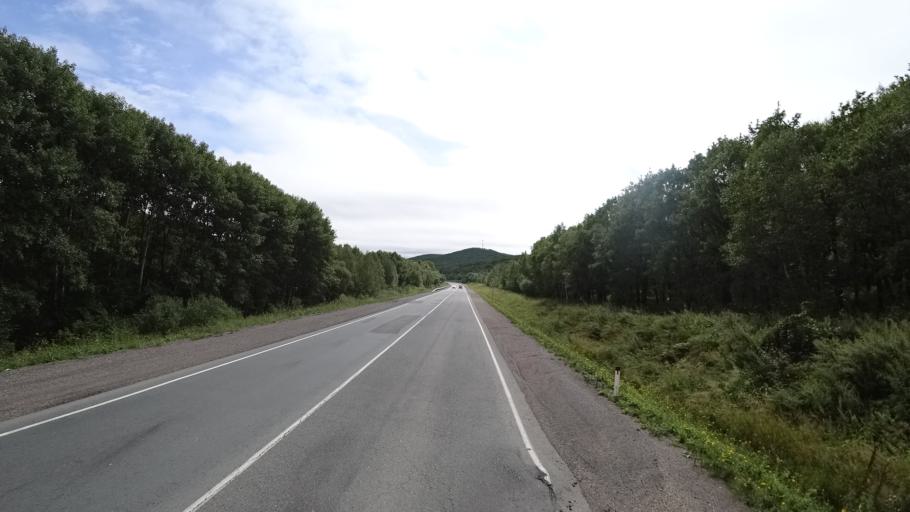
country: RU
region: Primorskiy
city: Lyalichi
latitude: 44.1197
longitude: 132.4197
